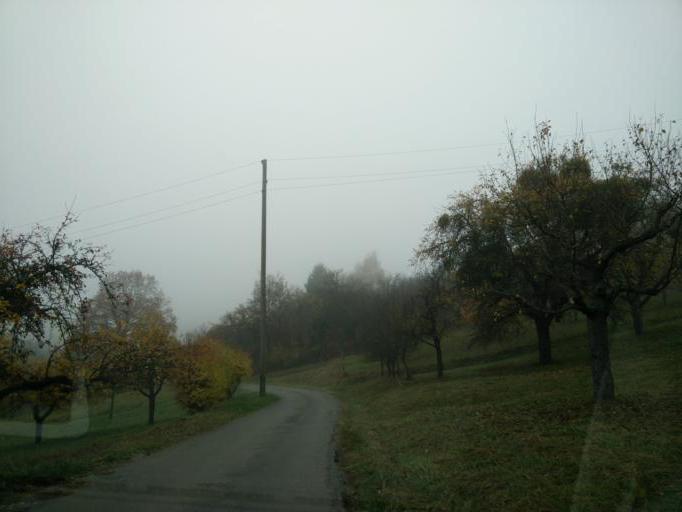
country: DE
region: Baden-Wuerttemberg
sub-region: Tuebingen Region
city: Tuebingen
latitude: 48.5411
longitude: 8.9796
